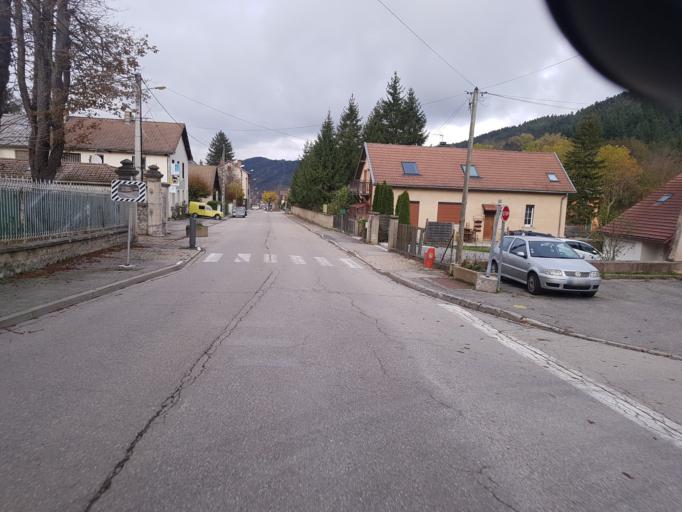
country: FR
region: Rhone-Alpes
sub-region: Departement de l'Isere
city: La Motte-Saint-Martin
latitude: 44.9119
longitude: 5.6322
